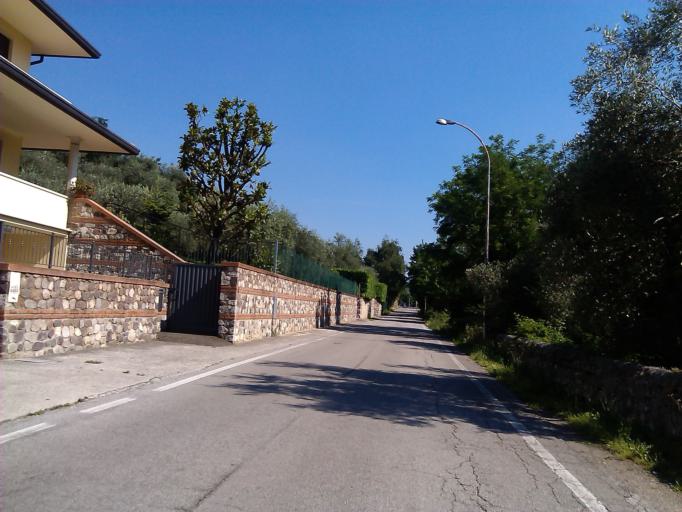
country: IT
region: Veneto
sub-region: Provincia di Vicenza
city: Pove del Grappa
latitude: 45.7975
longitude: 11.7253
